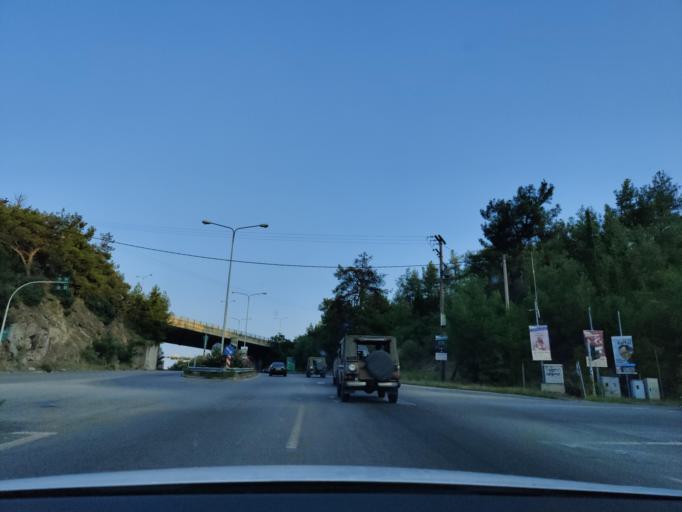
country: GR
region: East Macedonia and Thrace
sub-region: Nomos Kavalas
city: Amygdaleonas
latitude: 40.9437
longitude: 24.3739
